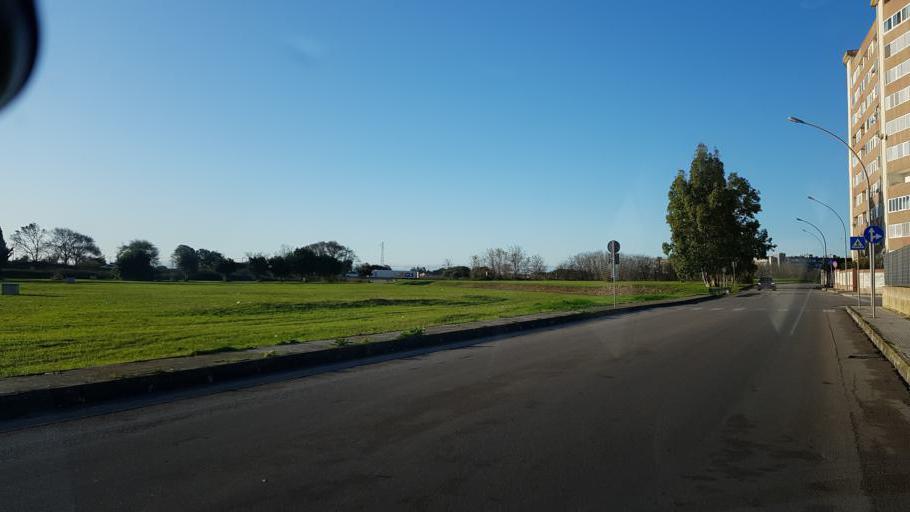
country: IT
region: Apulia
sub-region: Provincia di Brindisi
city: Brindisi
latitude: 40.6209
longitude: 17.9423
